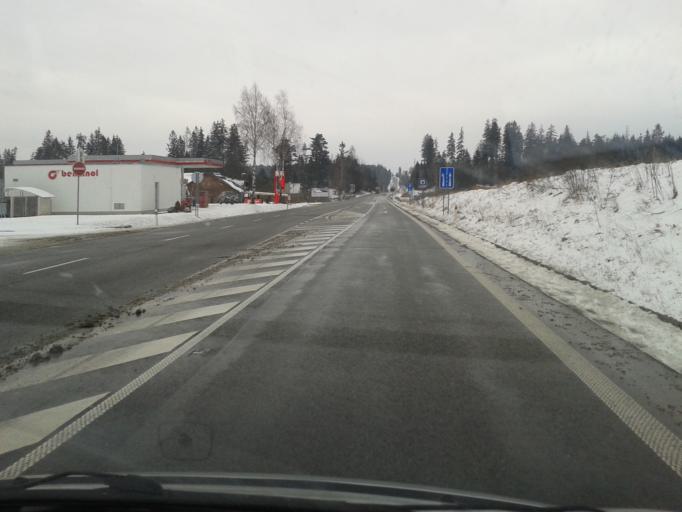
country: PL
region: Lesser Poland Voivodeship
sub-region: Powiat nowotarski
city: Chyzne
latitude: 49.4001
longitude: 19.6505
